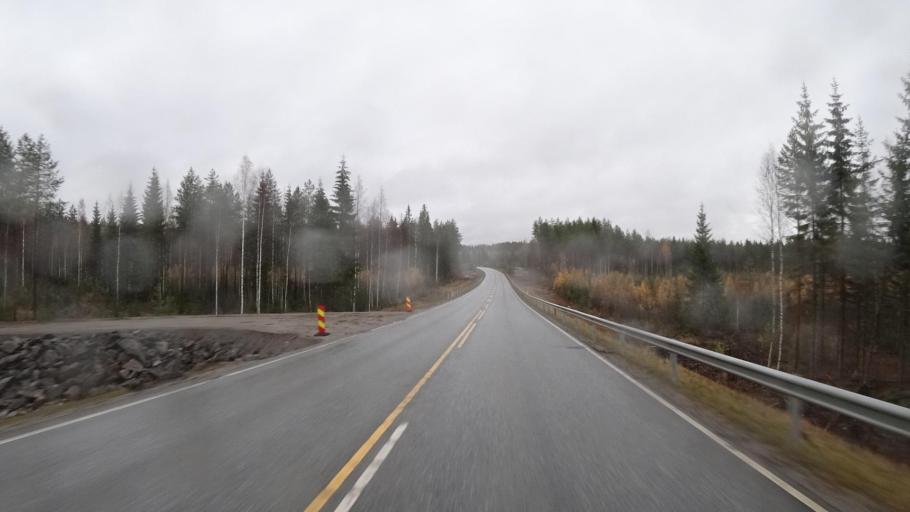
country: FI
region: Northern Savo
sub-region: Varkaus
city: Kangaslampi
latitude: 62.4583
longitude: 28.3085
